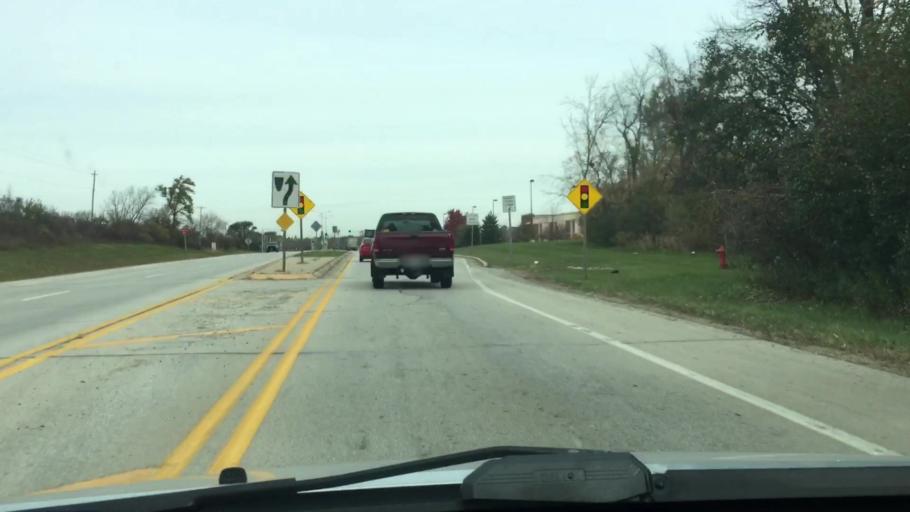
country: US
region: Wisconsin
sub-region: Milwaukee County
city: Franklin
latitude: 42.9015
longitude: -88.0392
